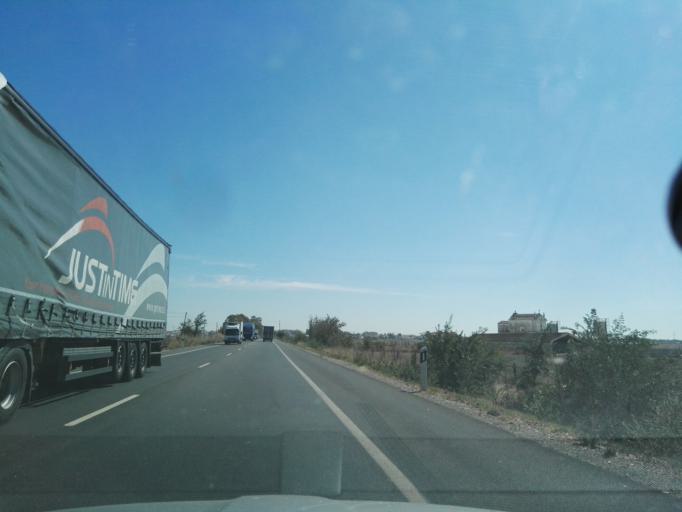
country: PT
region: Santarem
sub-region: Benavente
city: Samora Correia
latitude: 38.9294
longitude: -8.9059
